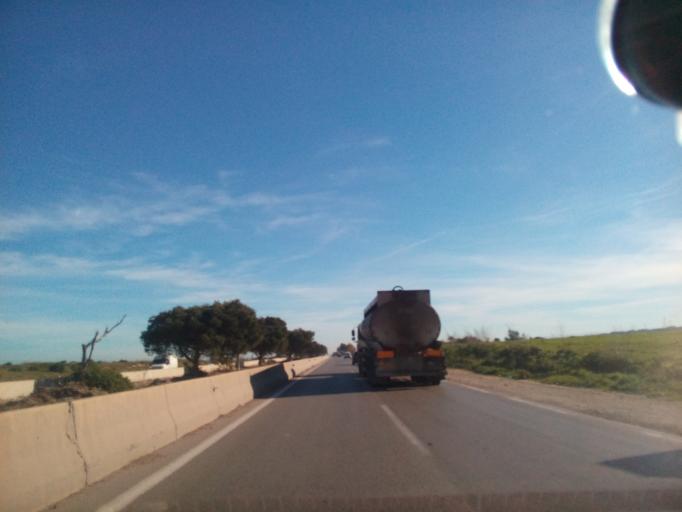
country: DZ
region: Oran
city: Ain el Bya
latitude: 35.7669
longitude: -0.2162
